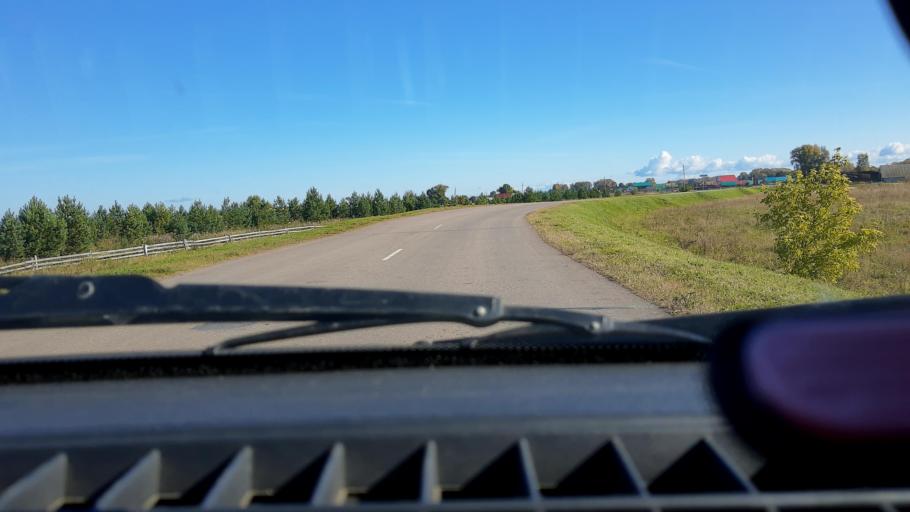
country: RU
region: Bashkortostan
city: Kushnarenkovo
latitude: 55.0877
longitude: 55.4790
